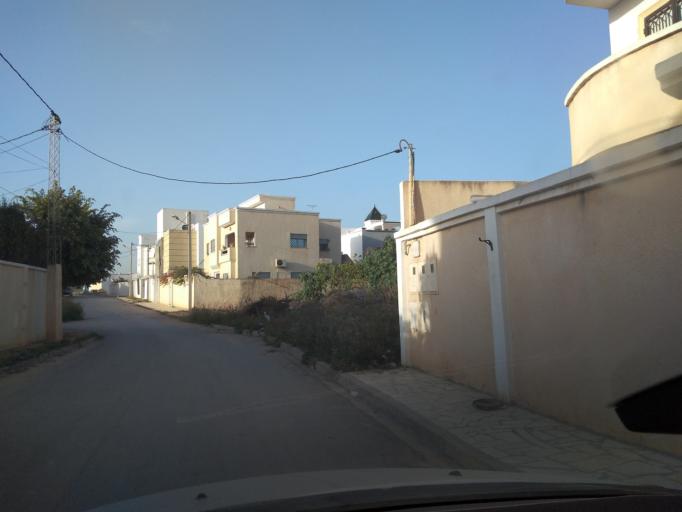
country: TN
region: Manouba
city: Manouba
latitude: 36.7944
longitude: 10.0853
